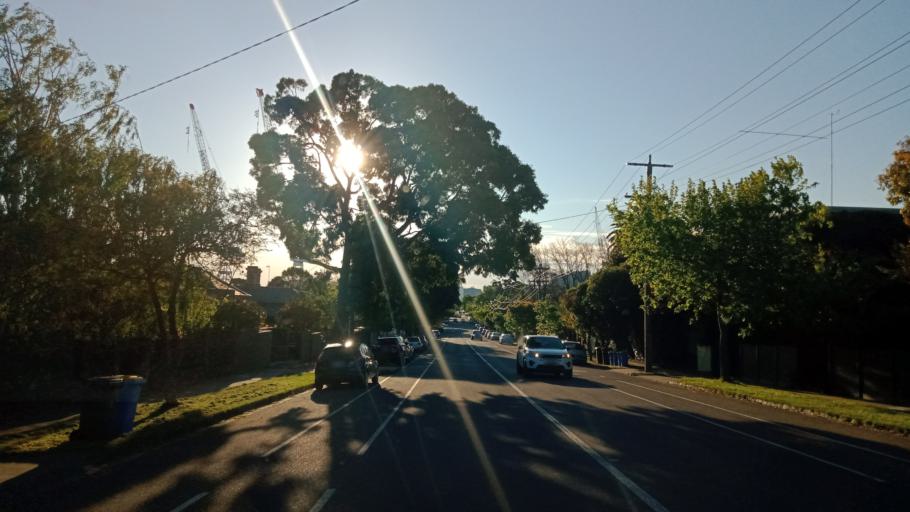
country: AU
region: Victoria
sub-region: Boroondara
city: Hawthorn East
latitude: -37.8248
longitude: 145.0532
